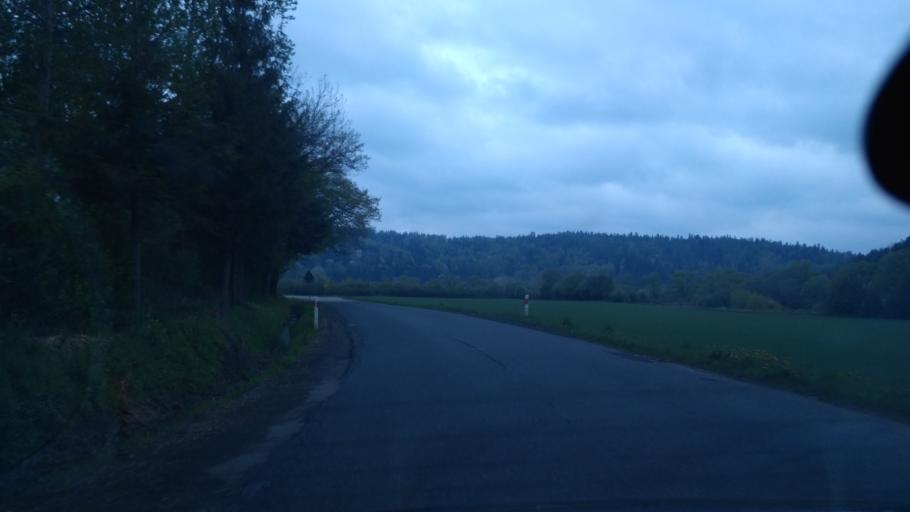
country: PL
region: Subcarpathian Voivodeship
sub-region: Powiat brzozowski
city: Nozdrzec
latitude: 49.7299
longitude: 22.2204
